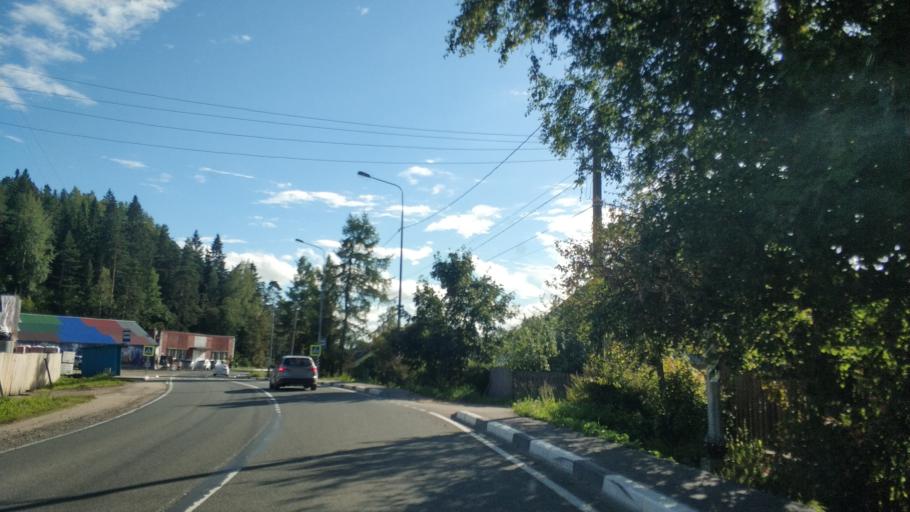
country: RU
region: Republic of Karelia
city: Lakhdenpokh'ya
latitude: 61.5263
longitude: 30.2018
